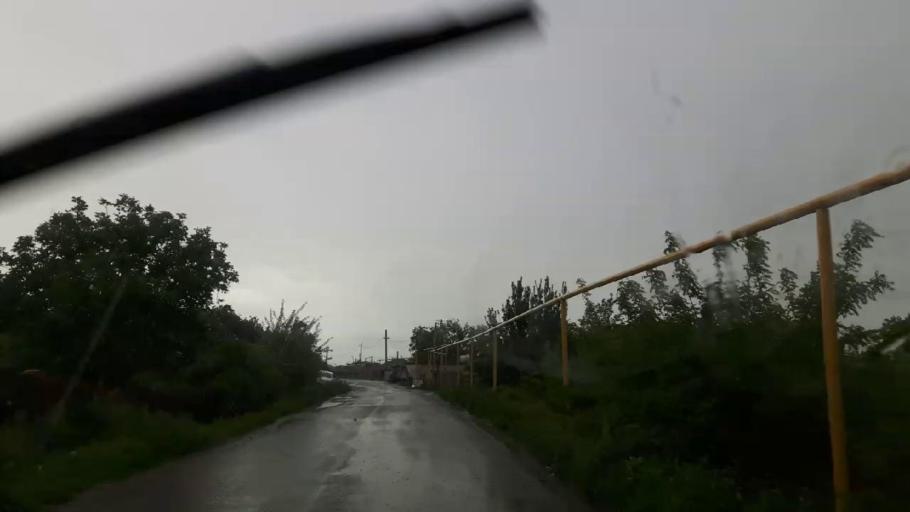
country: GE
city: Agara
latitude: 42.0159
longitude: 43.8463
